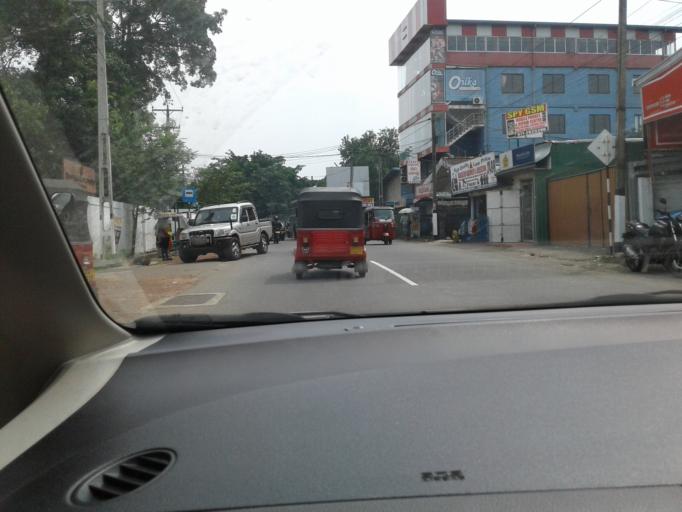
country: LK
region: Western
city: Maharagama
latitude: 6.8557
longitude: 79.9176
